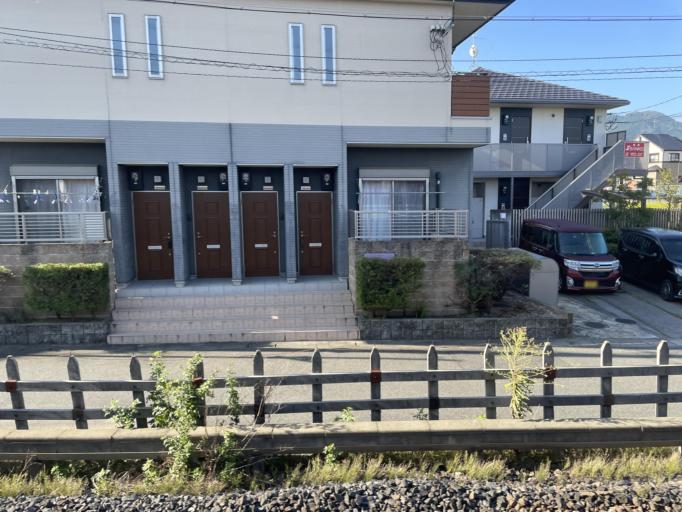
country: JP
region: Osaka
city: Kashihara
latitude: 34.5444
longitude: 135.6947
